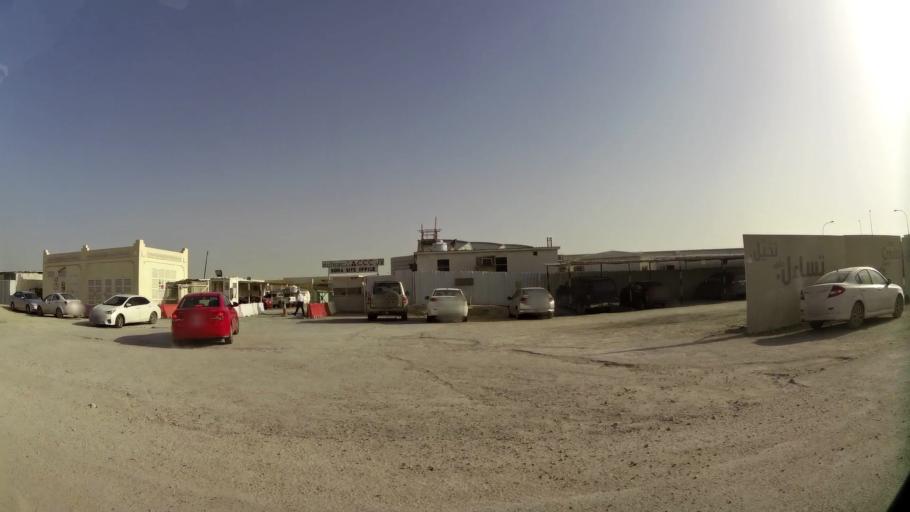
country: QA
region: Baladiyat ar Rayyan
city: Ar Rayyan
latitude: 25.3279
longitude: 51.4449
